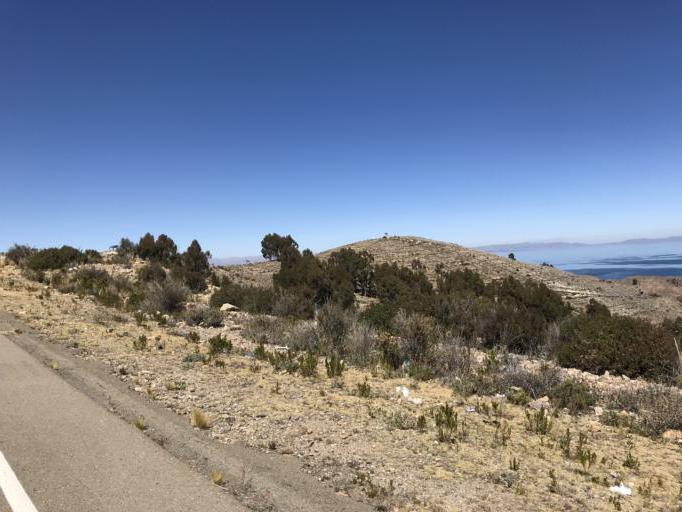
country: BO
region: La Paz
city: San Pedro
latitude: -16.1985
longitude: -68.9098
